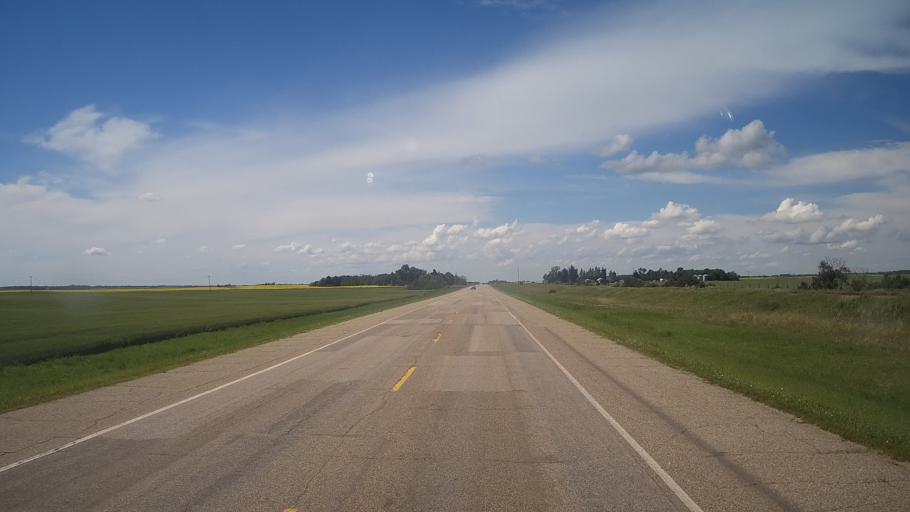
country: CA
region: Saskatchewan
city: Yorkton
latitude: 51.0873
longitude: -102.2563
